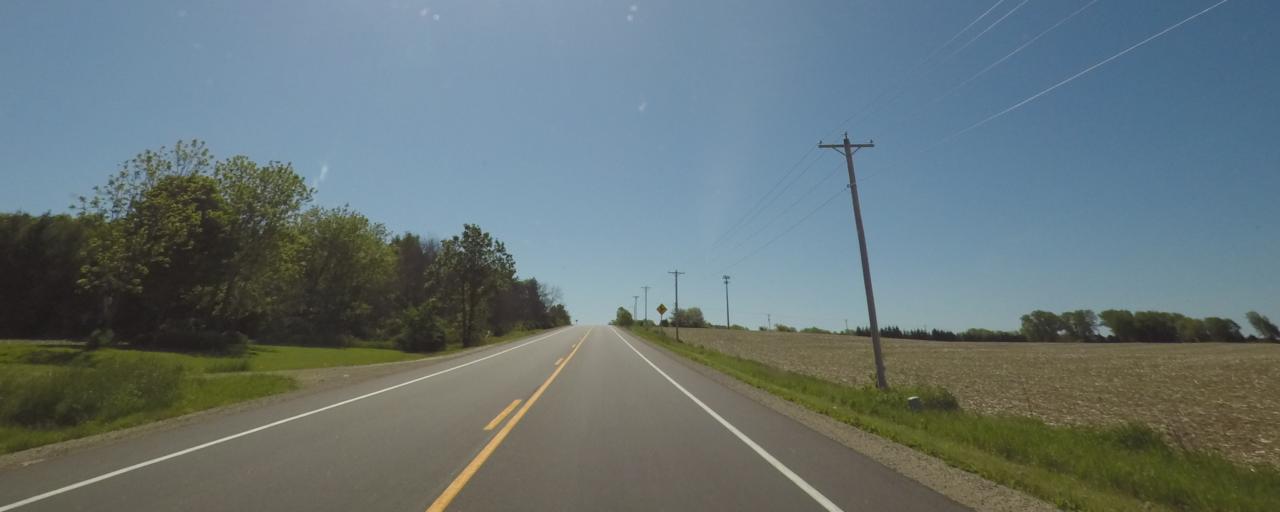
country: US
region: Wisconsin
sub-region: Dane County
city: Fitchburg
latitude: 42.9534
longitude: -89.4646
